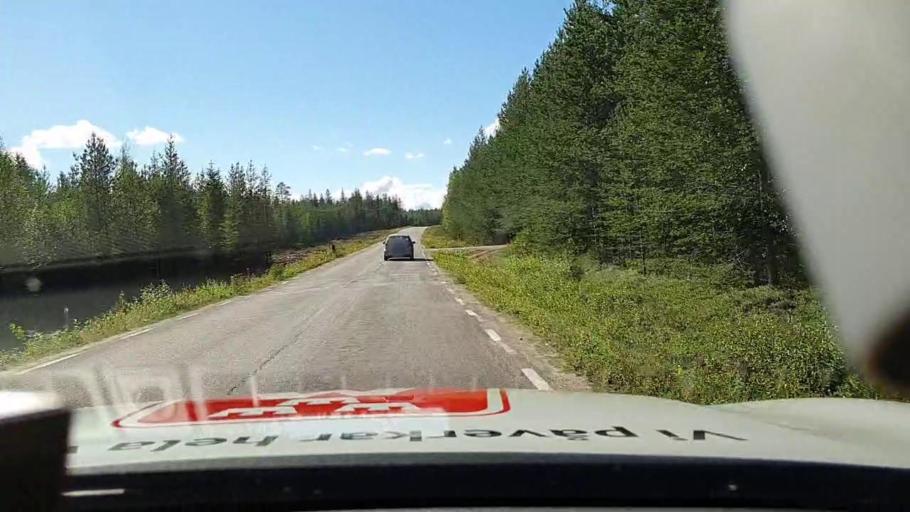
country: SE
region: Norrbotten
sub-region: Overkalix Kommun
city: OEverkalix
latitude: 66.2463
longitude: 22.9128
